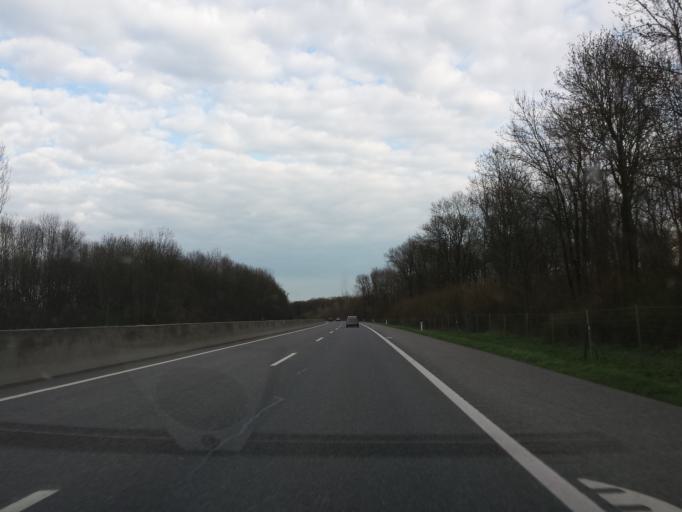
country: AT
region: Lower Austria
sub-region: Politischer Bezirk Tulln
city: Michelhausen
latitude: 48.3707
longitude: 15.9388
